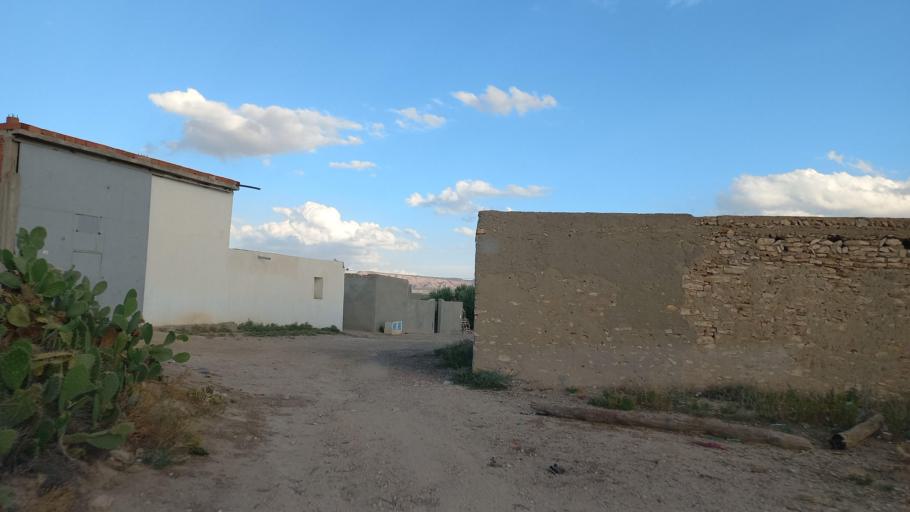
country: TN
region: Al Qasrayn
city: Sbiba
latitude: 35.3880
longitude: 9.0457
